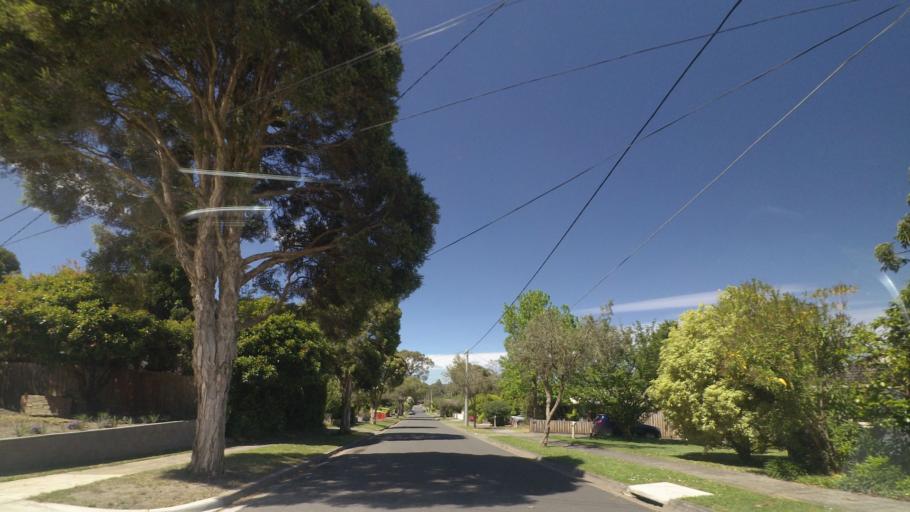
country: AU
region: Victoria
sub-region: Yarra Ranges
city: Kilsyth
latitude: -37.7962
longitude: 145.3229
